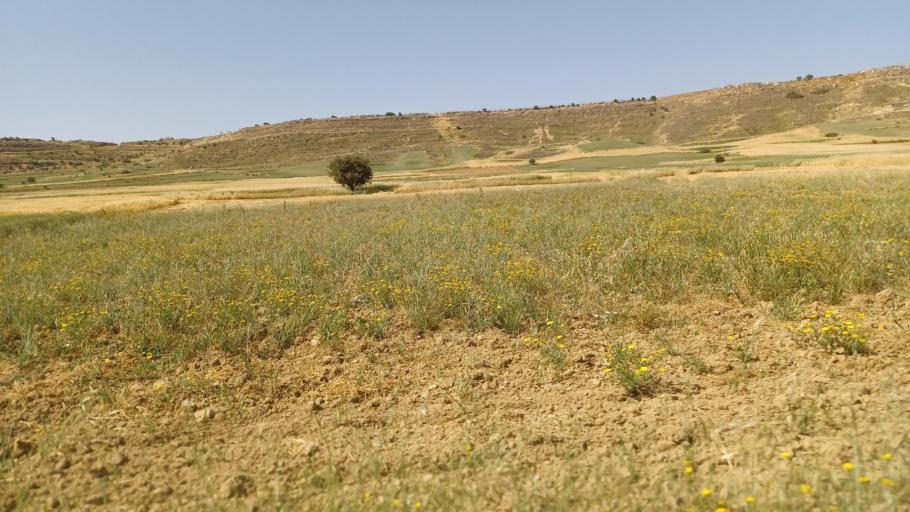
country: CY
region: Lefkosia
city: Mammari
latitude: 35.1711
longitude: 33.2289
